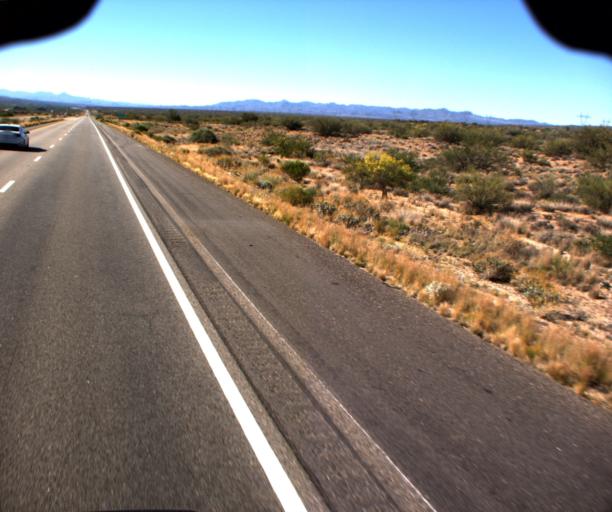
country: US
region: Arizona
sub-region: Mohave County
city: Kingman
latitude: 34.8732
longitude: -113.6458
